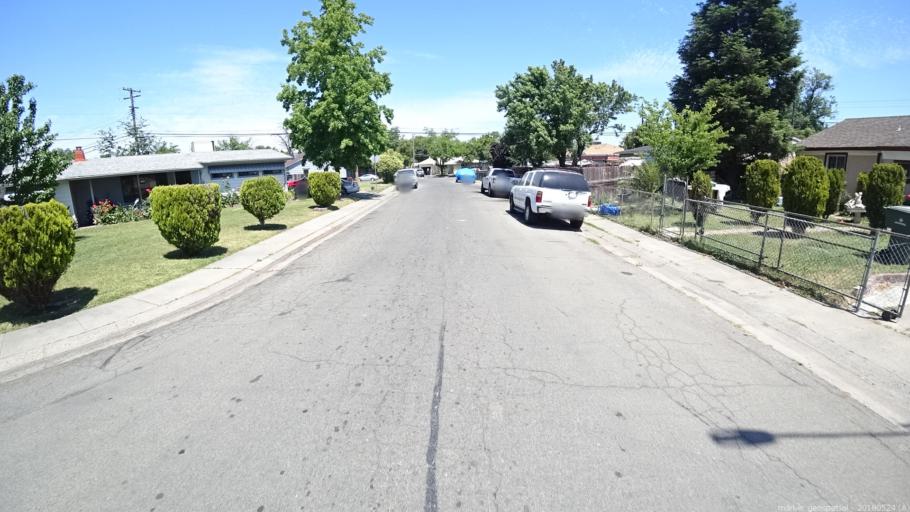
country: US
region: California
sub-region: Sacramento County
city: Sacramento
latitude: 38.6238
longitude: -121.4482
